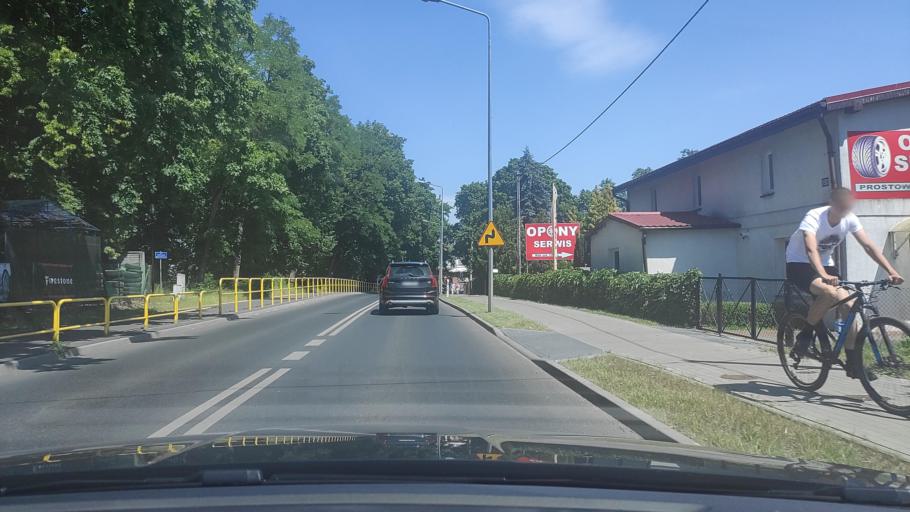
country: PL
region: Greater Poland Voivodeship
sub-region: Powiat pilski
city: Pila
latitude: 53.1726
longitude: 16.7406
